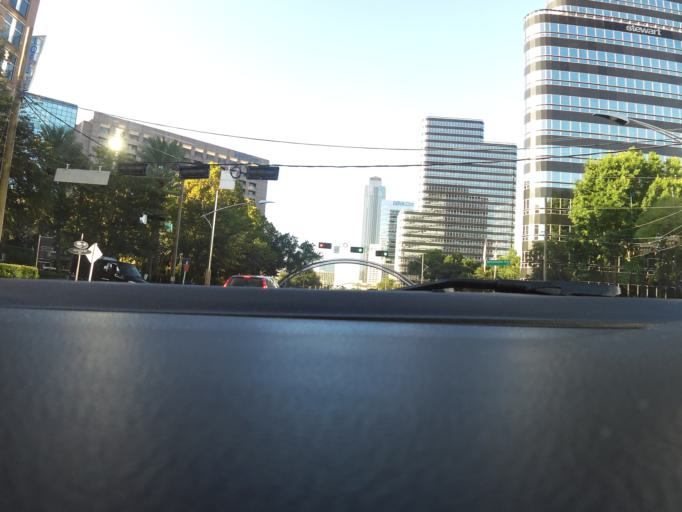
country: US
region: Texas
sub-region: Harris County
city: West University Place
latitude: 29.7471
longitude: -95.4612
